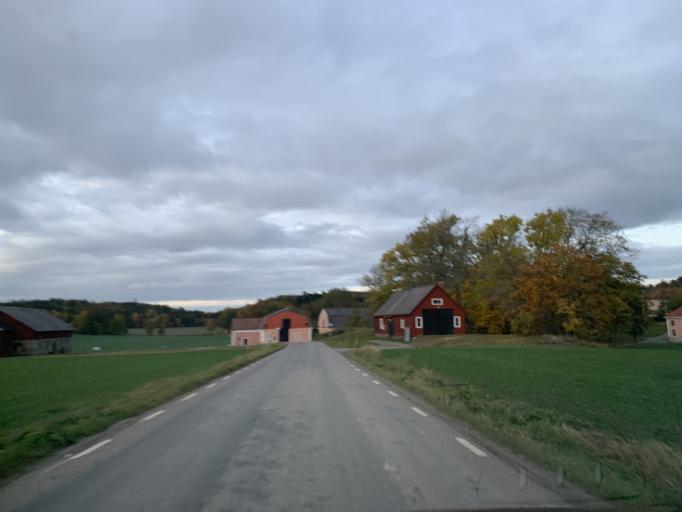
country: SE
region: Stockholm
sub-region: Nynashamns Kommun
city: Osmo
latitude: 58.9570
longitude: 17.7667
